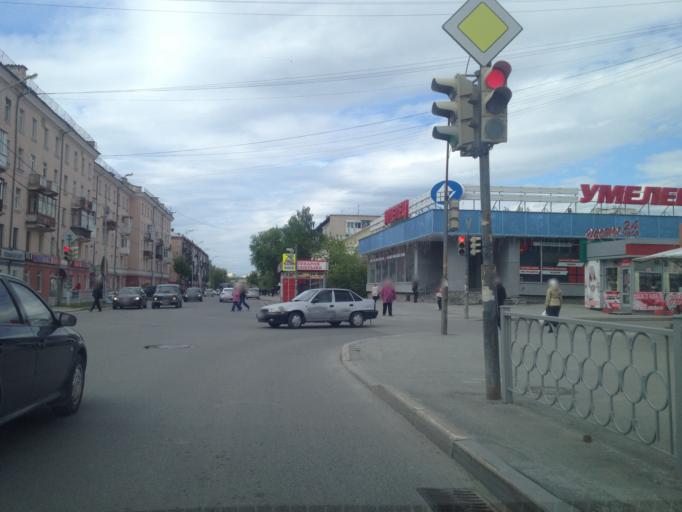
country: RU
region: Sverdlovsk
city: Yekaterinburg
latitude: 56.8331
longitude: 60.5525
